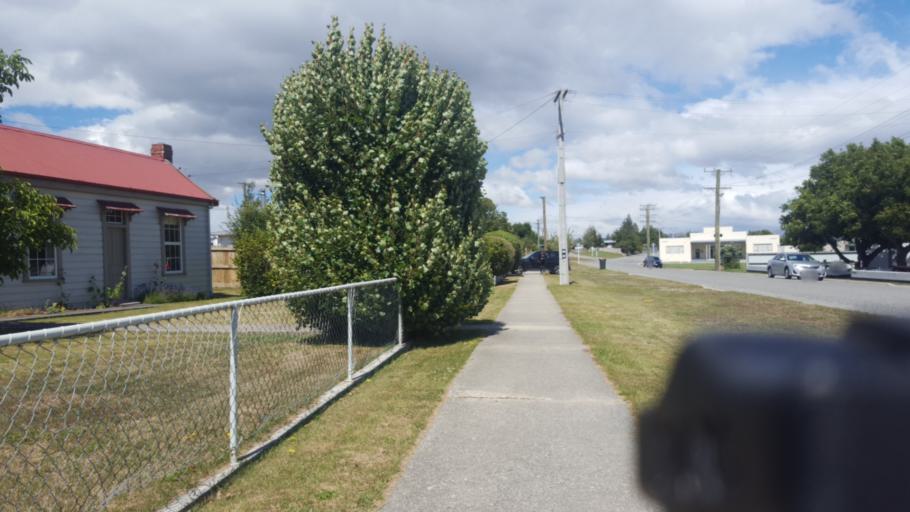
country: NZ
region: Otago
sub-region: Queenstown-Lakes District
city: Wanaka
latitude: -45.1873
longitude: 169.3188
